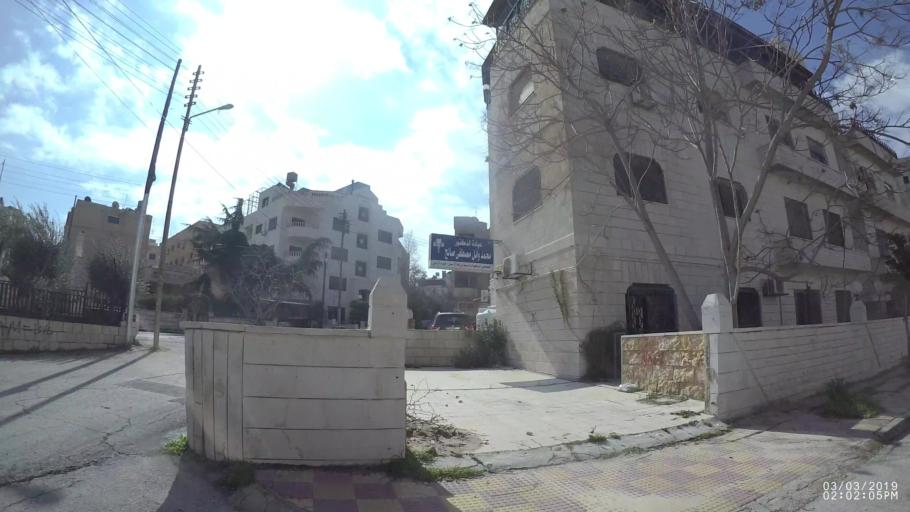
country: JO
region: Amman
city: Al Jubayhah
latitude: 31.9770
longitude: 35.8913
